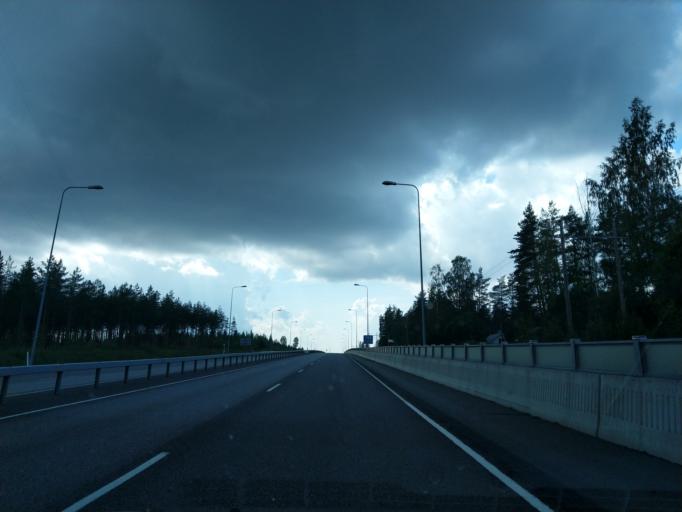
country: FI
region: South Karelia
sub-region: Imatra
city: Imatra
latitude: 61.1641
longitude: 28.6695
